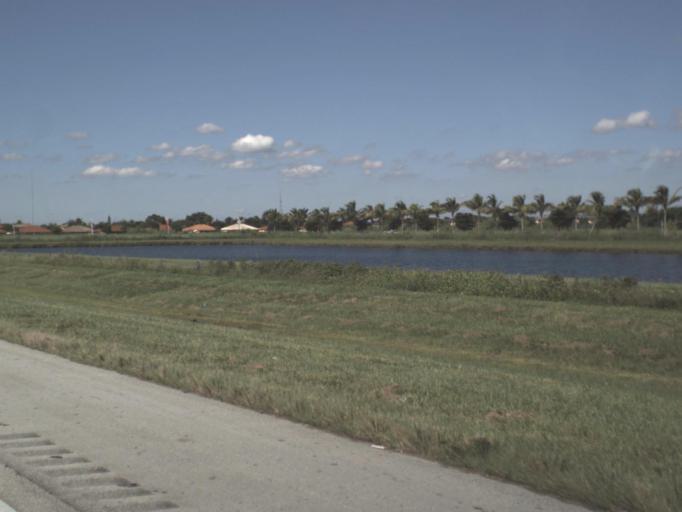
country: US
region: Florida
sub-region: Miami-Dade County
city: Princeton
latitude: 25.5305
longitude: -80.3834
